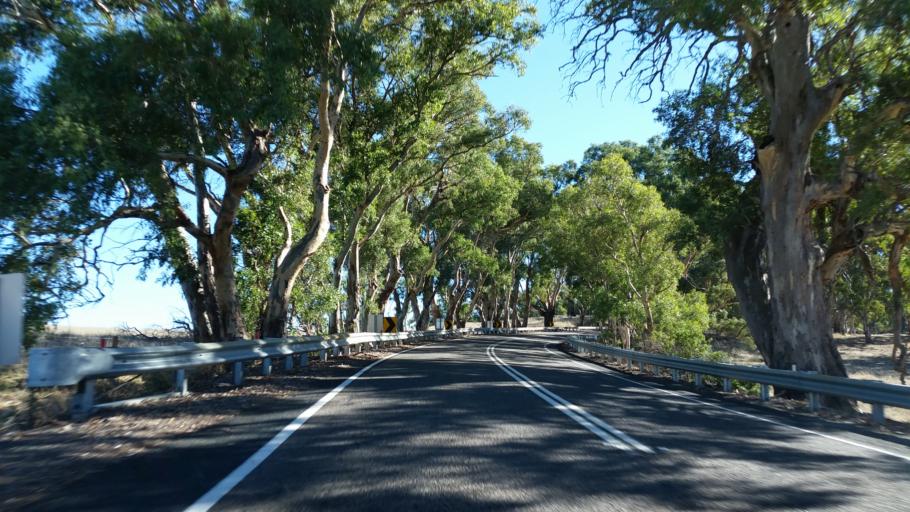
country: AU
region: South Australia
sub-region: Adelaide Hills
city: Birdwood
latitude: -34.8157
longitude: 139.0494
